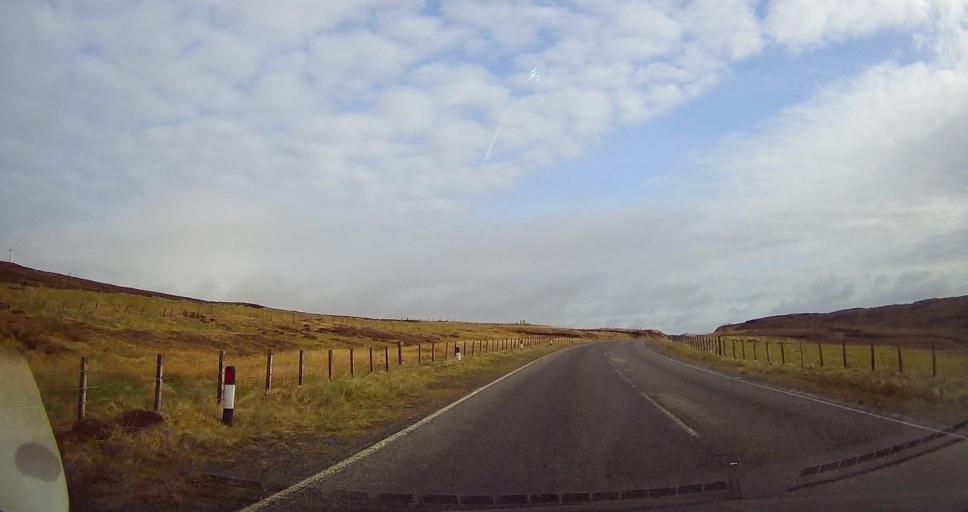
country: GB
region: Scotland
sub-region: Shetland Islands
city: Sandwick
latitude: 60.0857
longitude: -1.2322
